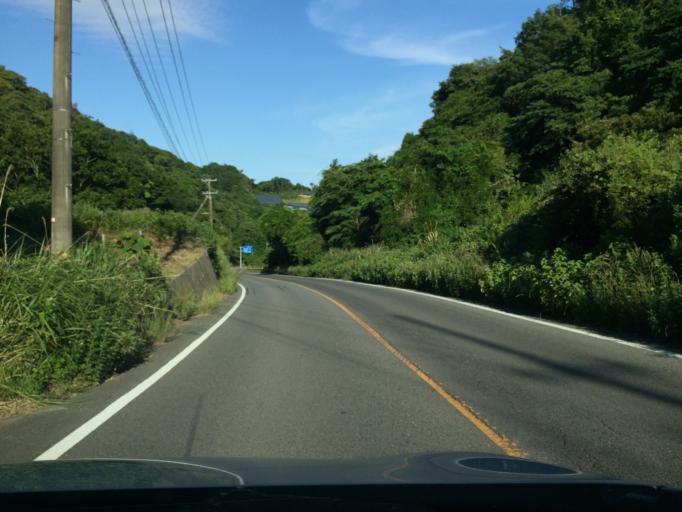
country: JP
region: Fukushima
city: Iwaki
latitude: 36.9784
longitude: 140.9491
